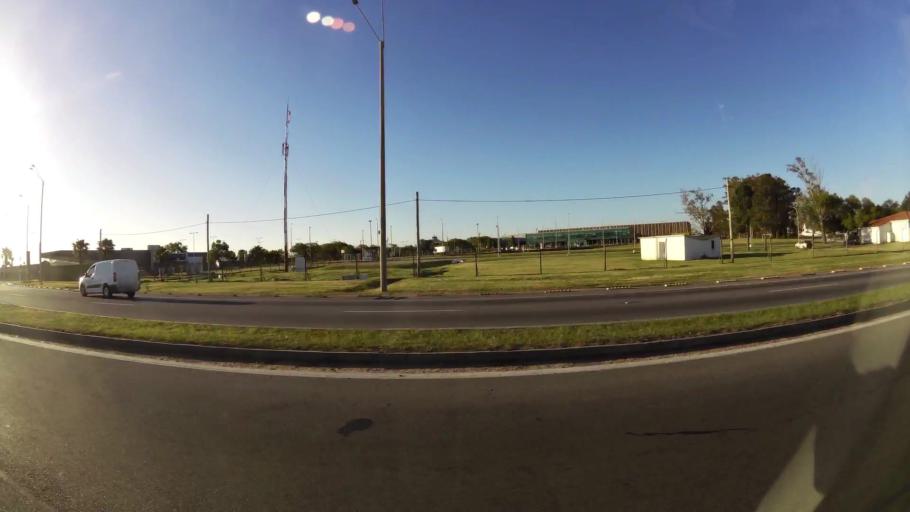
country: UY
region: Canelones
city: Barra de Carrasco
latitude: -34.8455
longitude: -56.0230
